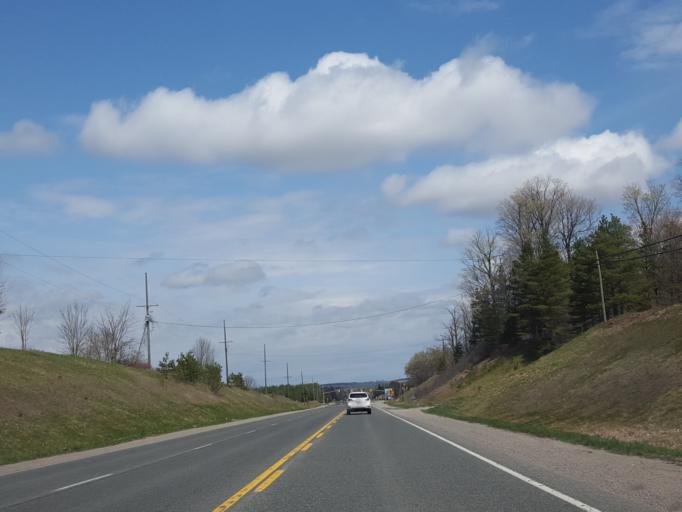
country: CA
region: Ontario
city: Newmarket
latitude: 44.1071
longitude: -79.3138
